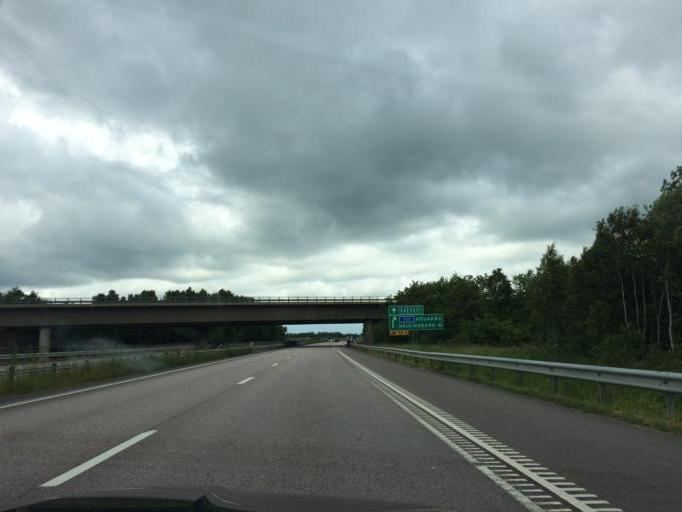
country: SE
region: Skane
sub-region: Helsingborg
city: Odakra
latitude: 56.0858
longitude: 12.7800
